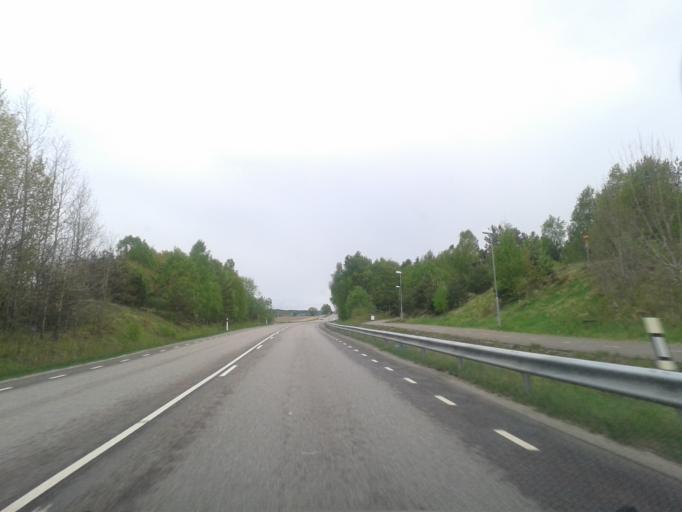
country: SE
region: Vaestra Goetaland
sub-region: Stenungsunds Kommun
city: Stora Hoga
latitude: 57.9974
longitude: 11.8273
